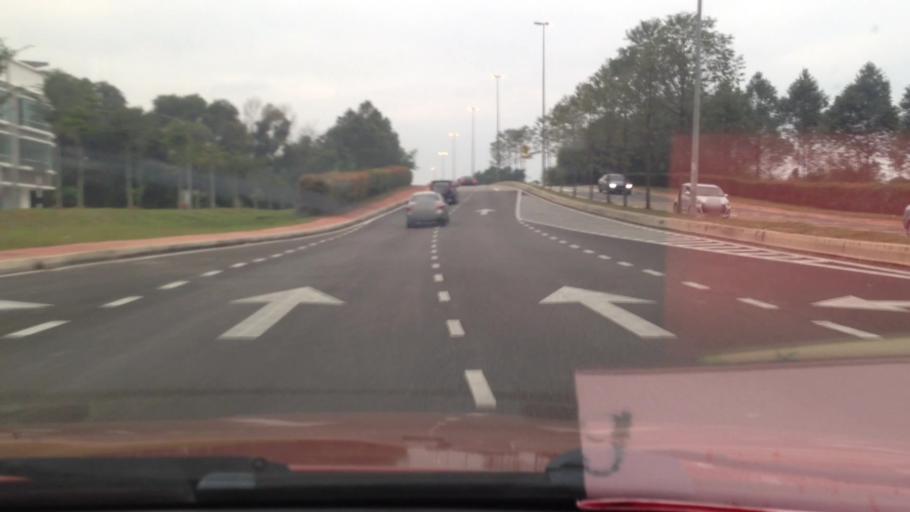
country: MY
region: Selangor
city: Subang Jaya
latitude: 3.0620
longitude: 101.5675
